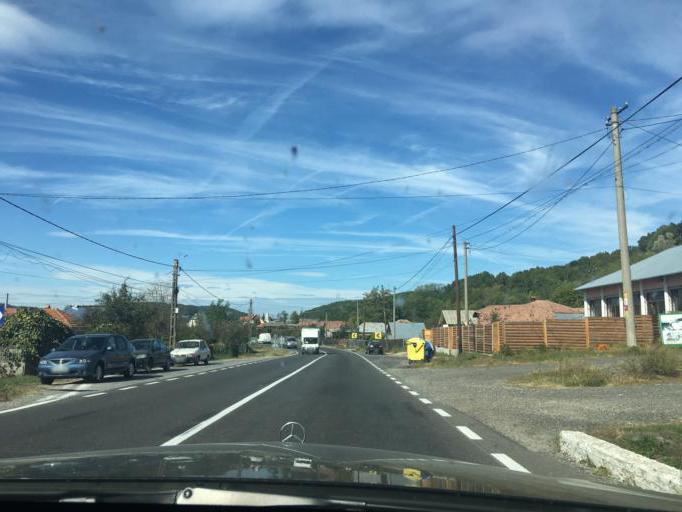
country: RO
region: Arges
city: Draganu-Olteni
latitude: 44.9353
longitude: 24.7089
